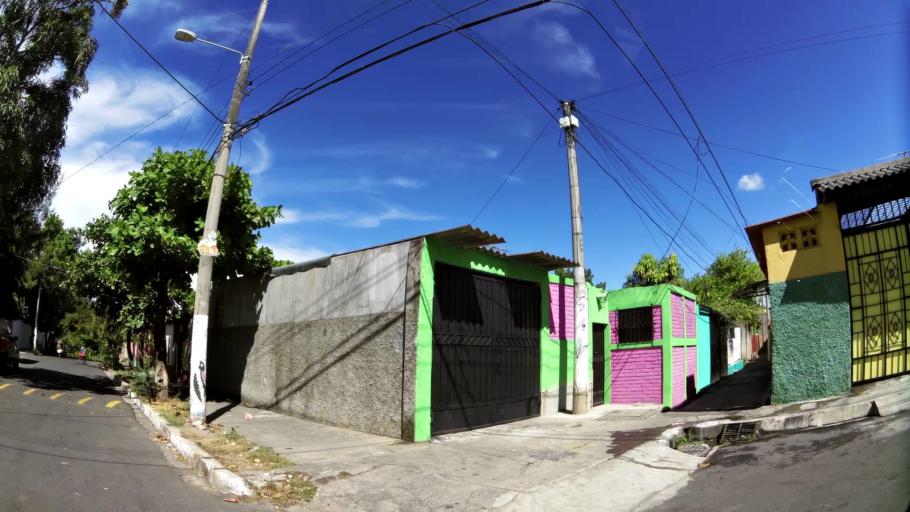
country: SV
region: San Salvador
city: Apopa
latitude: 13.8106
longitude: -89.1779
